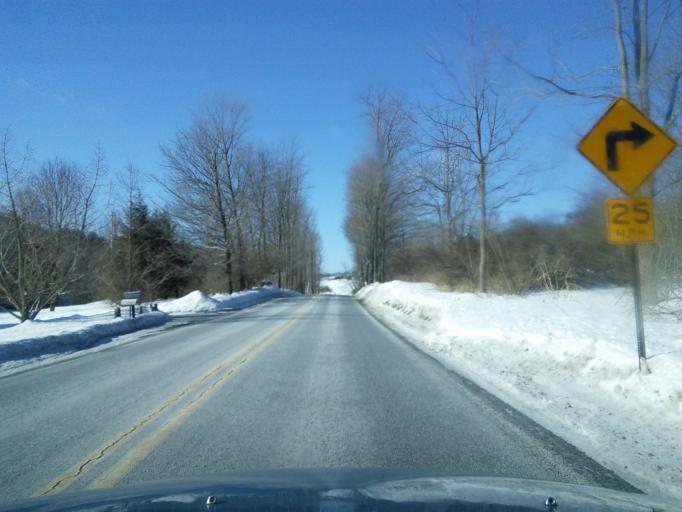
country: US
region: Pennsylvania
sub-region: Centre County
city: Park Forest Village
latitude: 40.8482
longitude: -77.9041
